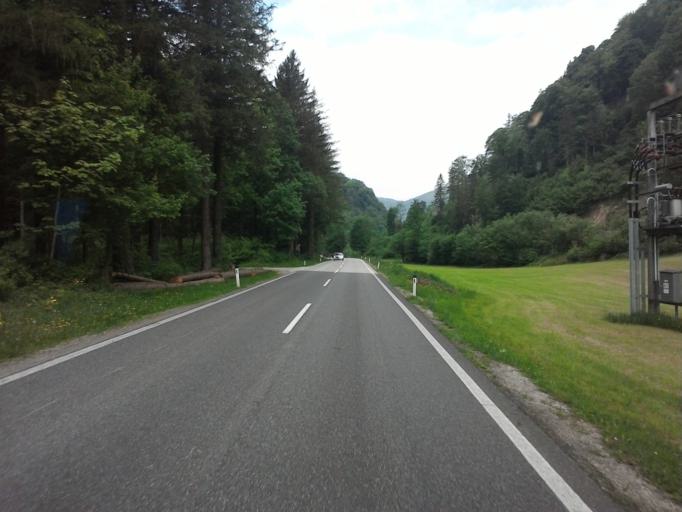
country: AT
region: Upper Austria
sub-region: Politischer Bezirk Steyr-Land
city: Weyer
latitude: 47.8611
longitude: 14.6129
